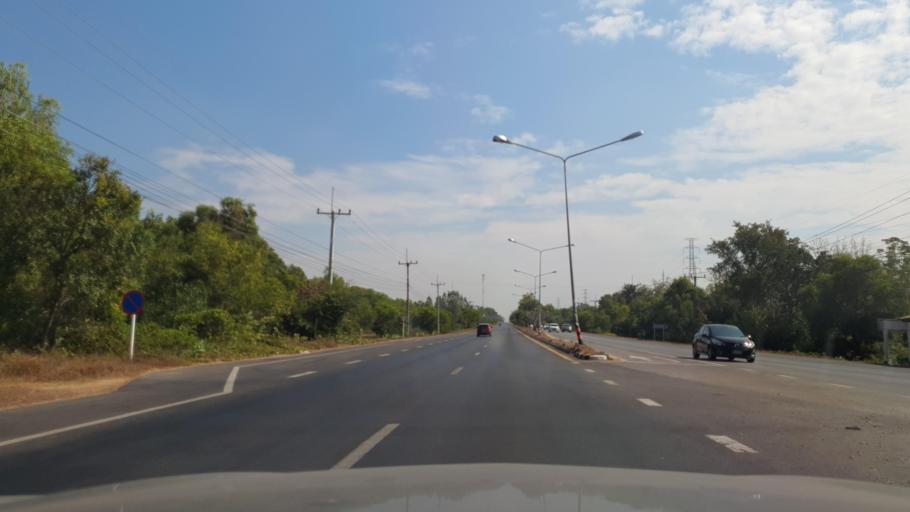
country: TH
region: Maha Sarakham
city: Kantharawichai
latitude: 16.3893
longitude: 103.2644
